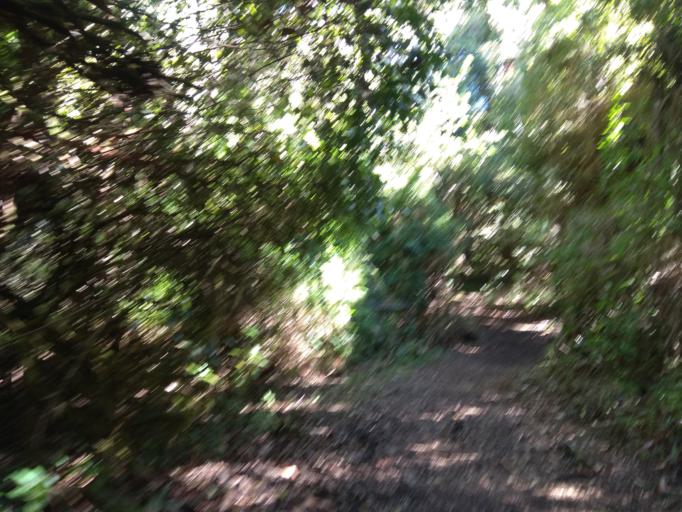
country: CR
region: Heredia
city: Santo Domingo
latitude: 10.1321
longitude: -84.1183
